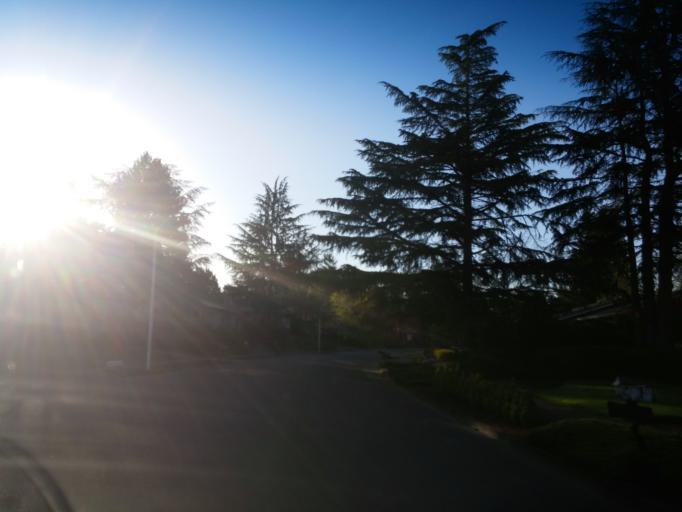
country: US
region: Oregon
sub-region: Washington County
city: Cedar Hills
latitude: 45.5050
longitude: -122.7907
